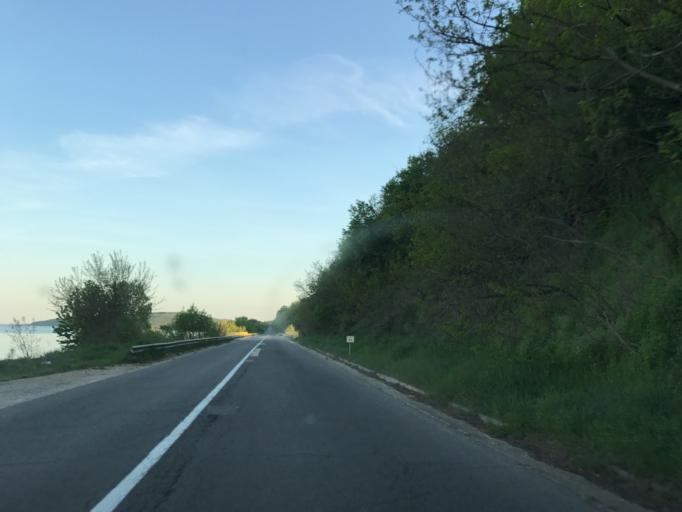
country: RO
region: Mehedinti
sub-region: Comuna Gogosu
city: Ostrovu Mare
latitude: 44.4637
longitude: 22.4507
